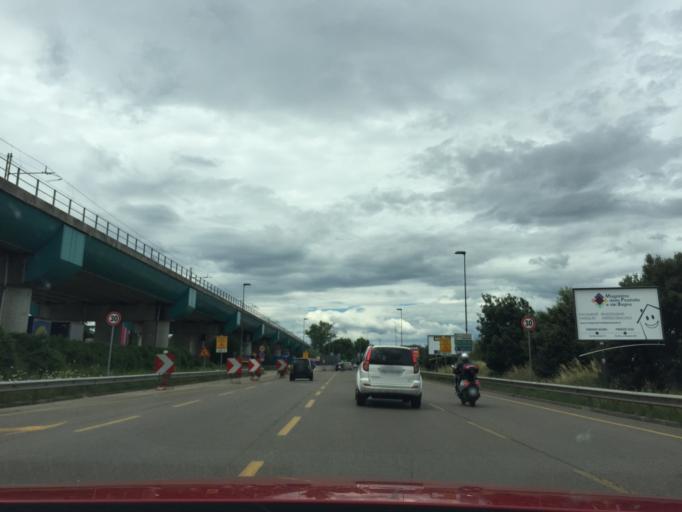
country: IT
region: Tuscany
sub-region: Province of Florence
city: Sesto Fiorentino
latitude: 43.8011
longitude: 11.2089
